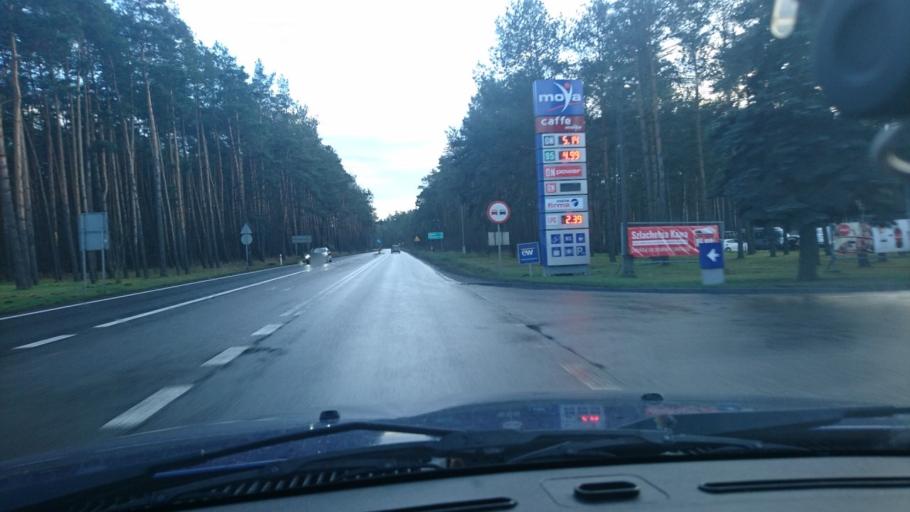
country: PL
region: Greater Poland Voivodeship
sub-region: Powiat kepinski
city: Kepno
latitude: 51.3408
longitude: 17.9525
